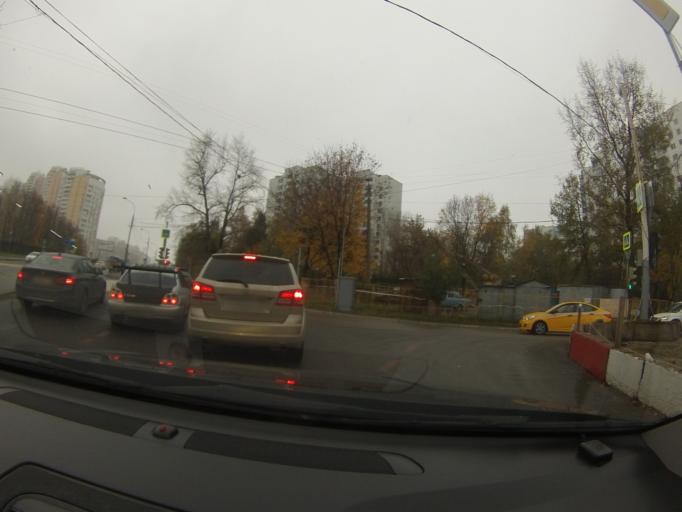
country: RU
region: Moscow
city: Nikol'skoye
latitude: 55.6875
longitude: 37.4867
